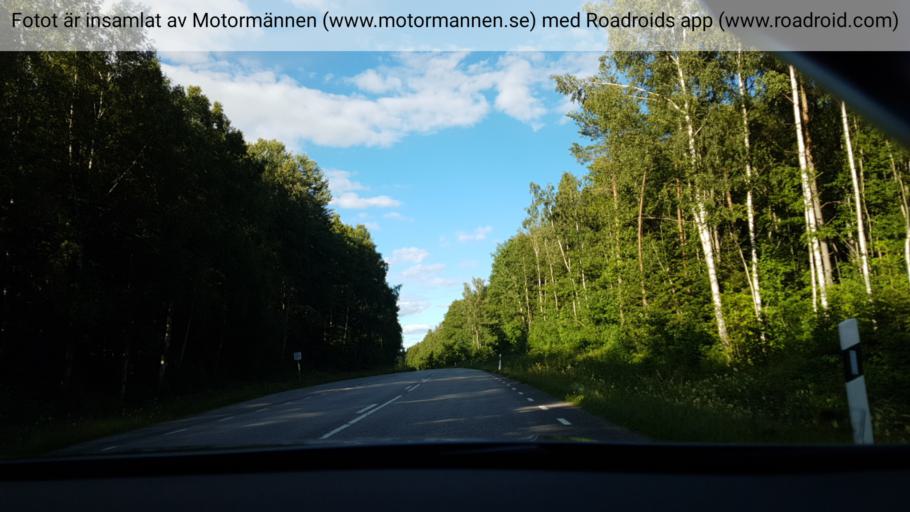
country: SE
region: Vaestra Goetaland
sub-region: Karlsborgs Kommun
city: Molltorp
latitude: 58.4805
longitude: 14.3480
